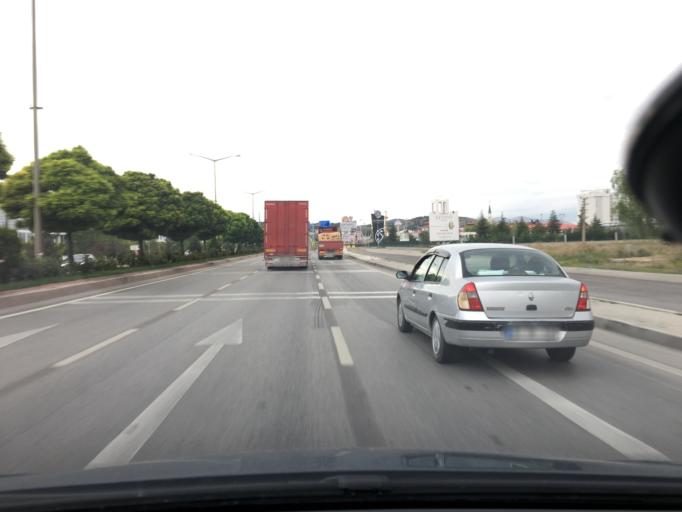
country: TR
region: Afyonkarahisar
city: Afyonkarahisar
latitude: 38.7886
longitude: 30.4621
